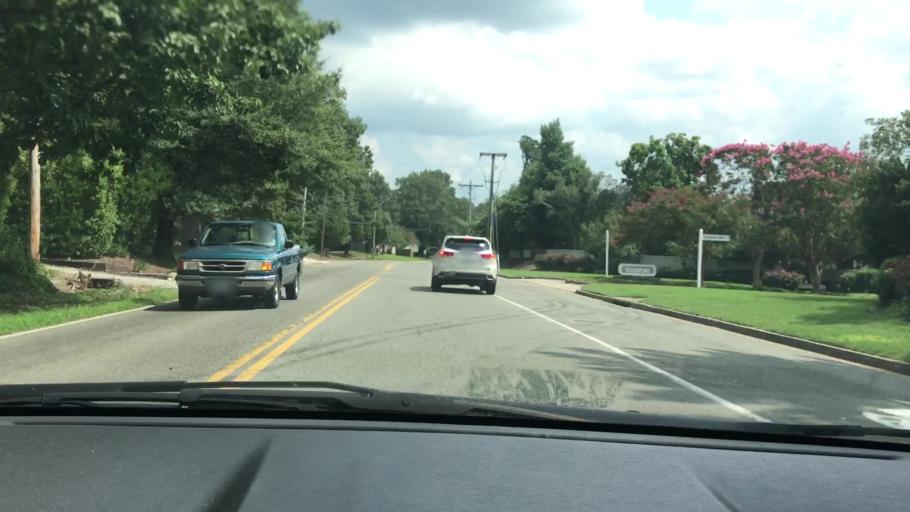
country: US
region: Virginia
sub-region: Henrico County
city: Tuckahoe
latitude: 37.5847
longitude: -77.5575
